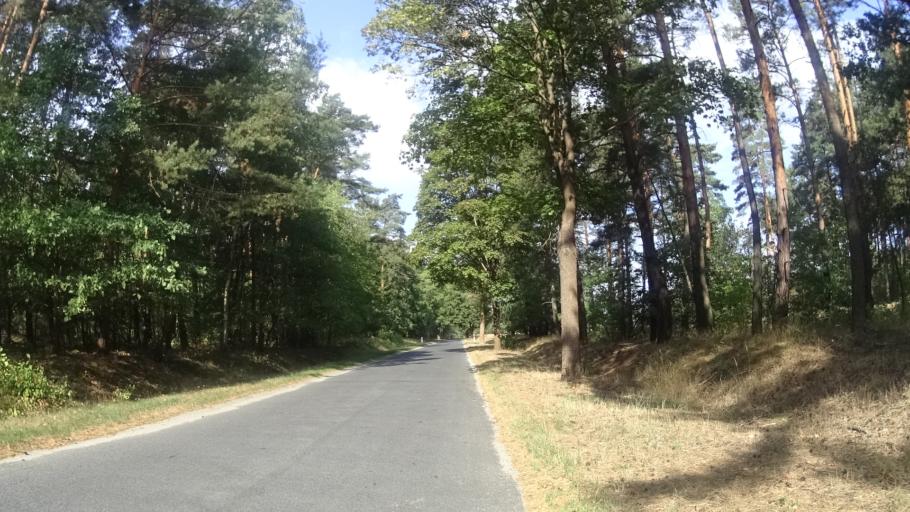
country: PL
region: Lubusz
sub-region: Powiat zarski
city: Przewoz
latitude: 51.4988
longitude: 14.8539
